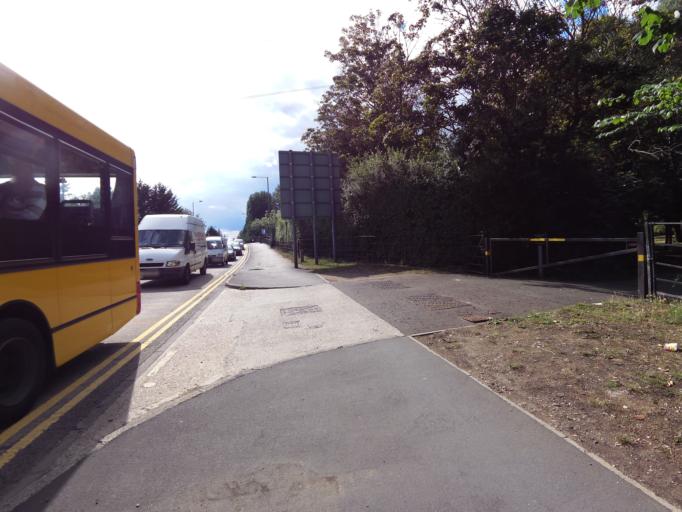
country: GB
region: England
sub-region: Essex
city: Waltham Abbey
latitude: 51.6870
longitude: -0.0104
